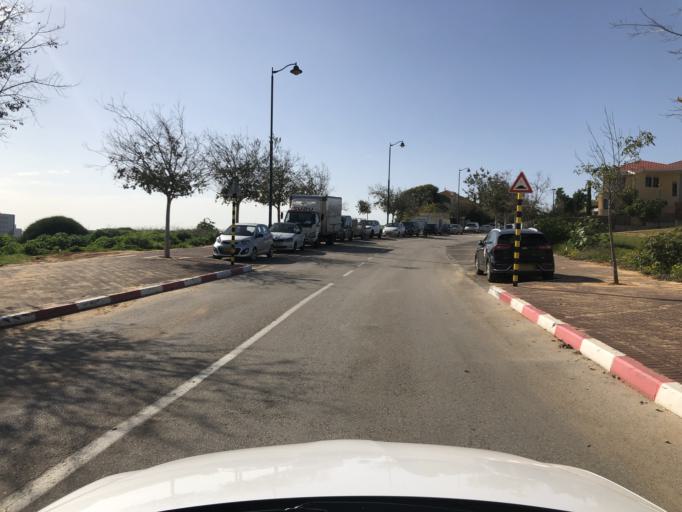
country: IL
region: Central District
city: Ness Ziona
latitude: 31.9094
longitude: 34.7900
